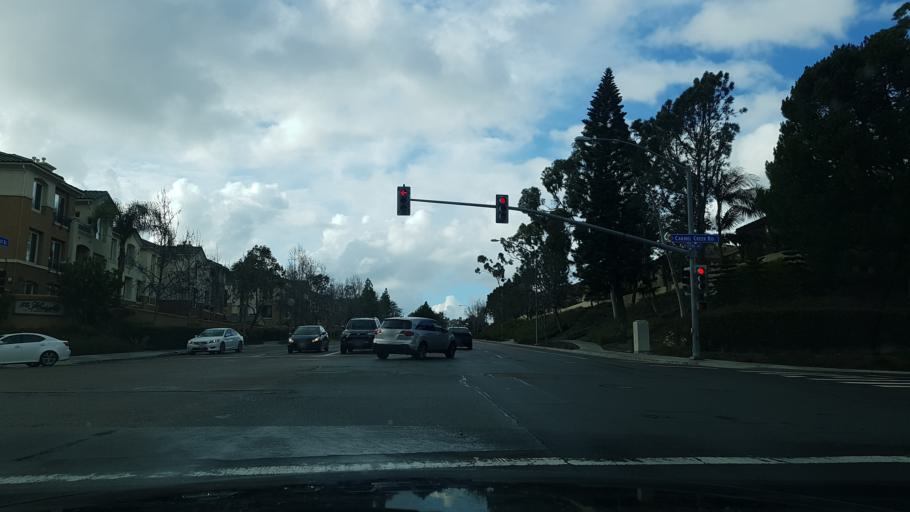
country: US
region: California
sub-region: San Diego County
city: Del Mar
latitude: 32.9470
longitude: -117.2267
